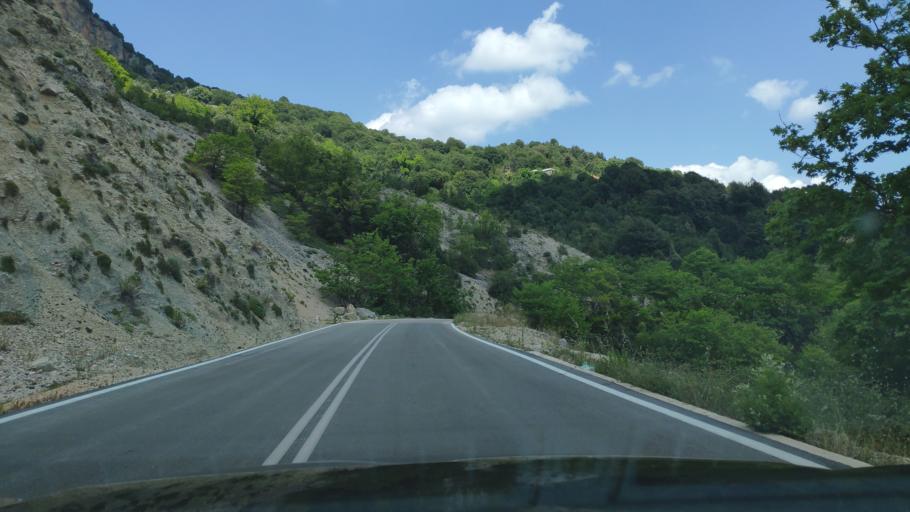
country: GR
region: Epirus
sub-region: Nomos Artas
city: Agios Dimitrios
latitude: 39.3467
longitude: 21.0041
